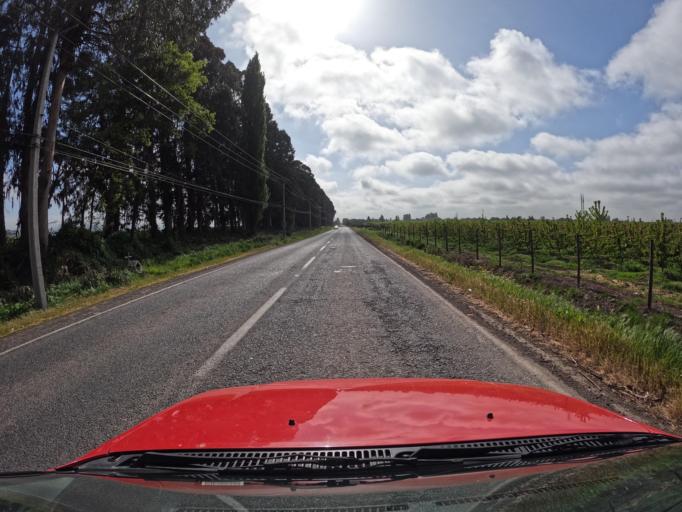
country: CL
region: Maule
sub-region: Provincia de Curico
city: Teno
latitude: -34.8665
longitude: -71.2086
